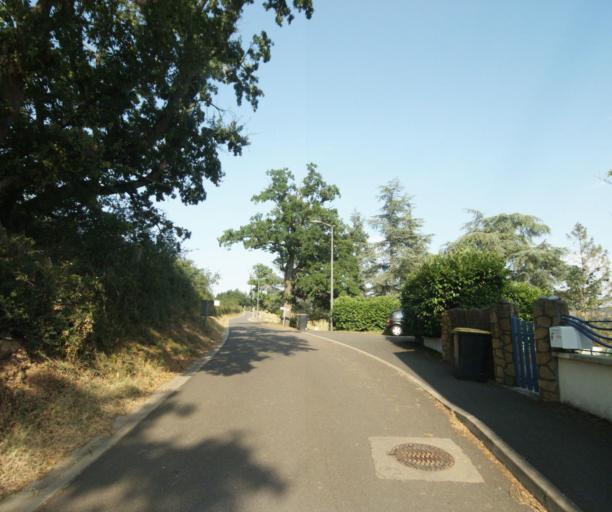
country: FR
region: Rhone-Alpes
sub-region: Departement du Rhone
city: Savigny
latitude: 45.8172
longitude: 4.5859
